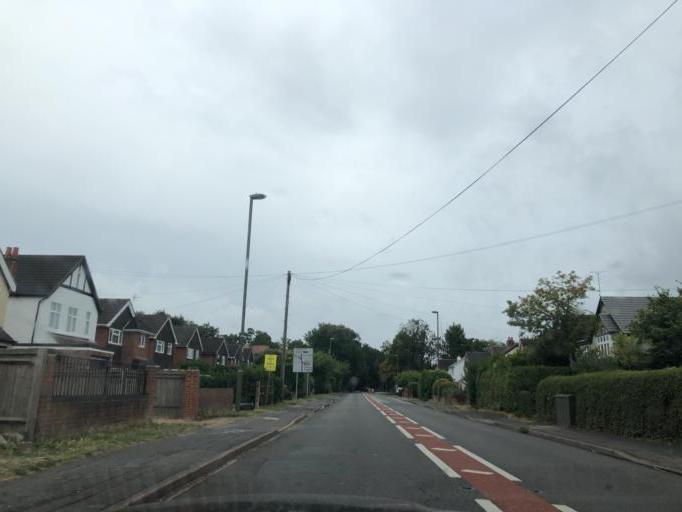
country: GB
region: England
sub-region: Hampshire
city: Farnborough
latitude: 51.2901
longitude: -0.7258
